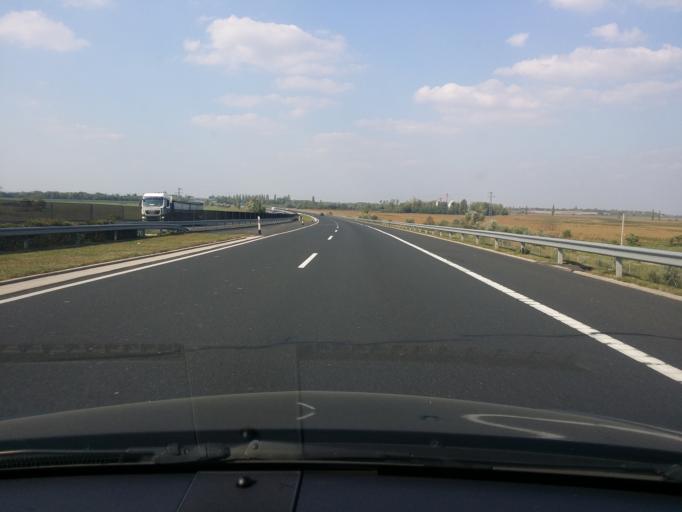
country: HU
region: Fejer
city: Adony
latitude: 47.1142
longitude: 18.8393
